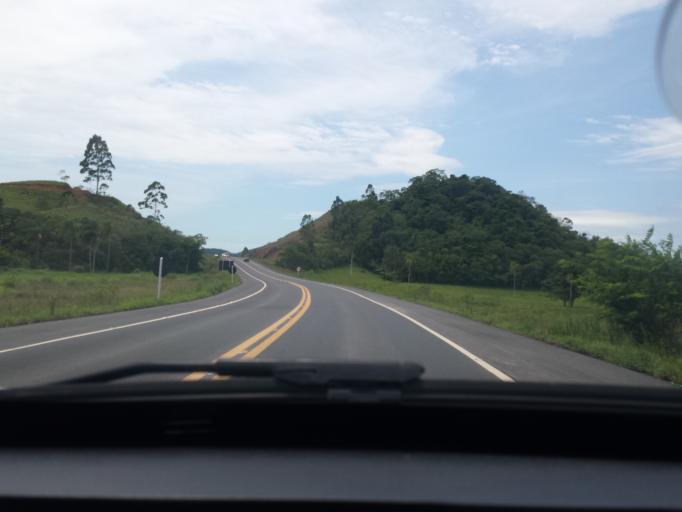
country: BR
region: Santa Catarina
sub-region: Gaspar
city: Gaspar
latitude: -26.8815
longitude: -48.8376
